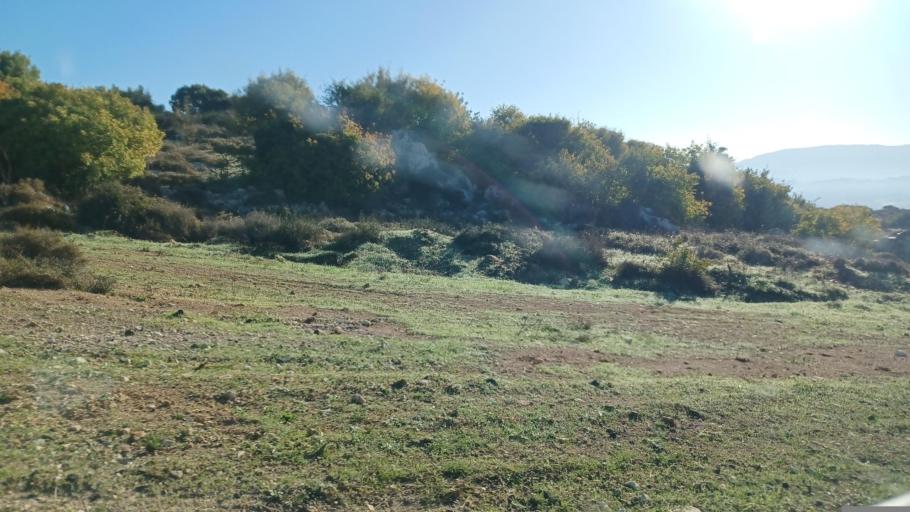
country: CY
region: Pafos
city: Polis
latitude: 34.9833
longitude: 32.5128
